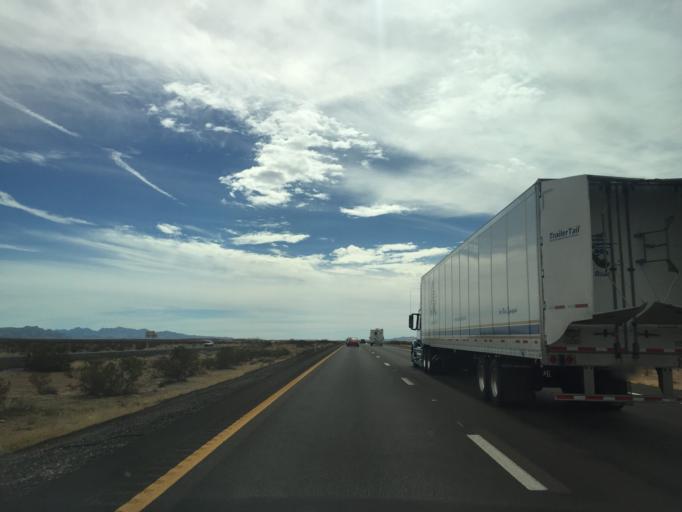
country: US
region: Nevada
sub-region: Clark County
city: Moapa Town
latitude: 36.5877
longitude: -114.6500
